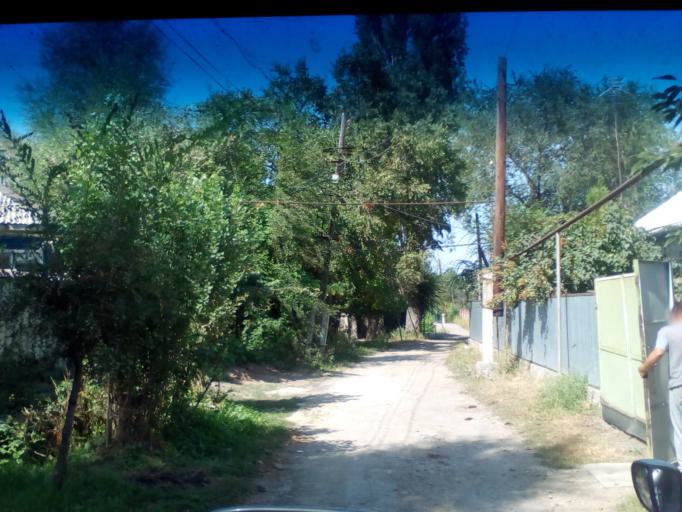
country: KZ
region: Almaty Oblysy
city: Burunday
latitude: 43.1580
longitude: 76.4086
